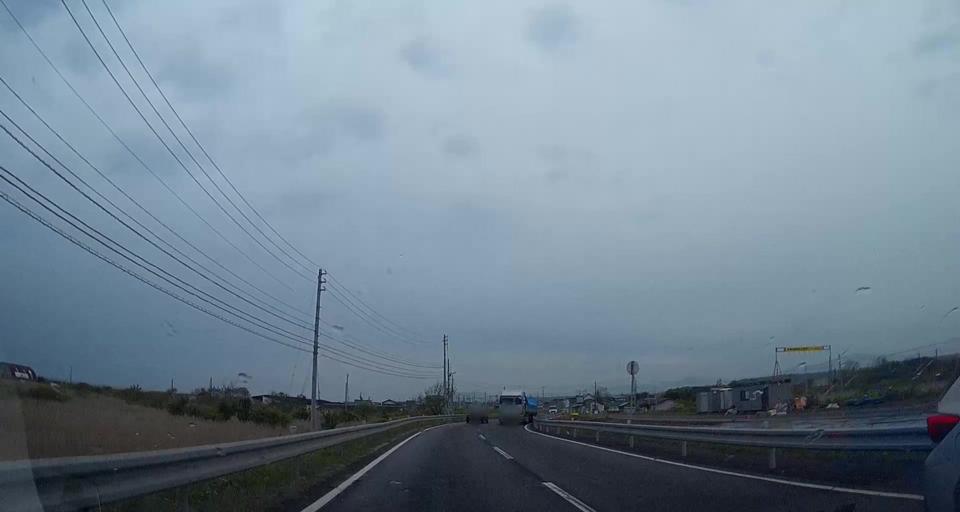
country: JP
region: Hokkaido
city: Shiraoi
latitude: 42.5790
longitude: 141.4220
